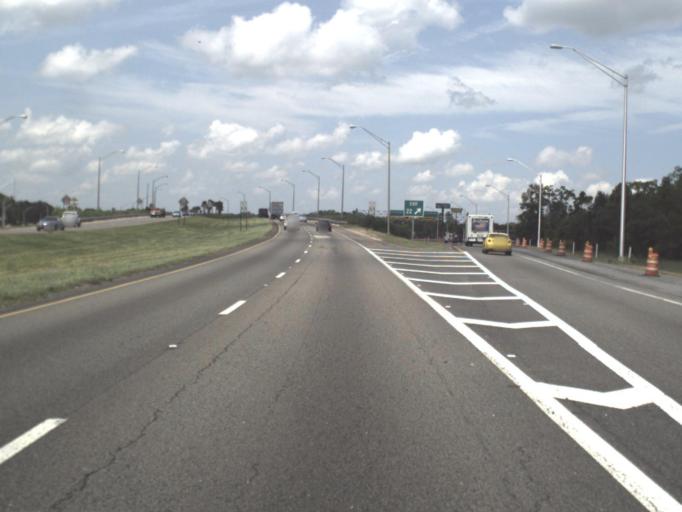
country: US
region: Florida
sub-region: Duval County
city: Jacksonville
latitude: 30.3320
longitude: -81.7627
